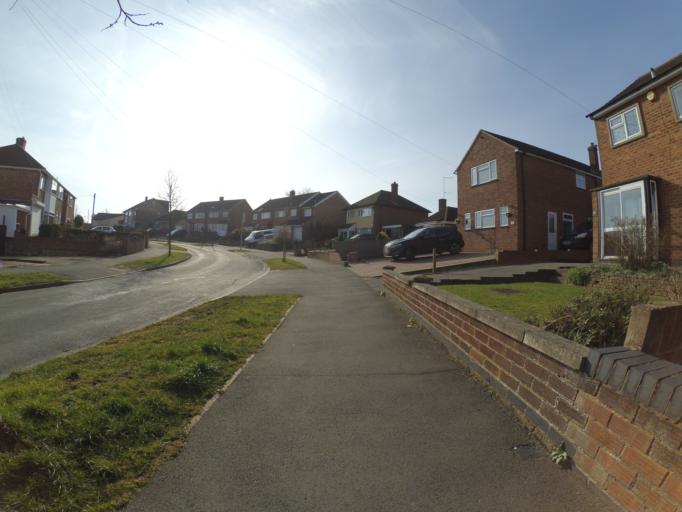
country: GB
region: England
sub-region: Warwickshire
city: Rugby
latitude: 52.3675
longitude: -1.2332
